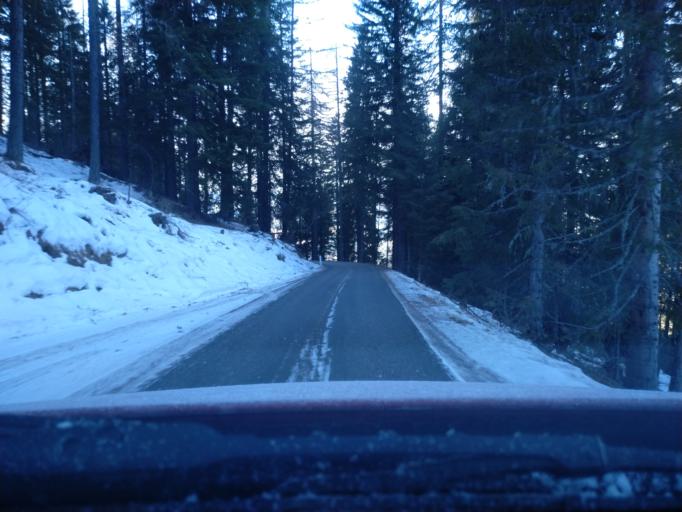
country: AT
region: Carinthia
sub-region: Politischer Bezirk Villach Land
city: Arriach
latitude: 46.7118
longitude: 13.9020
